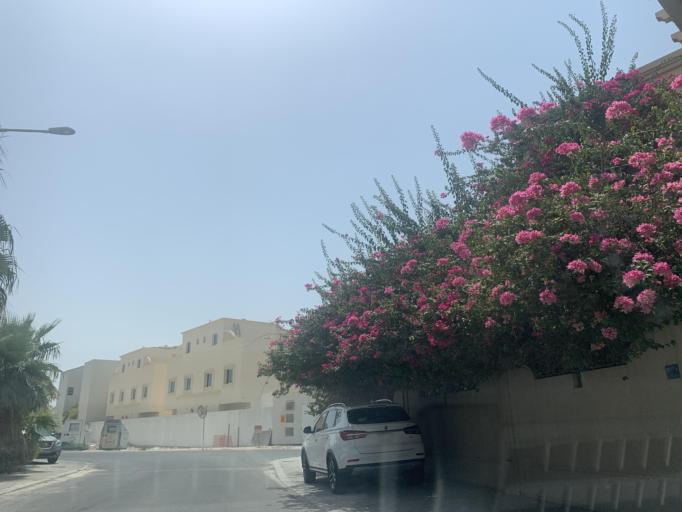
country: BH
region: Northern
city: Madinat `Isa
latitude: 26.1893
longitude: 50.4923
